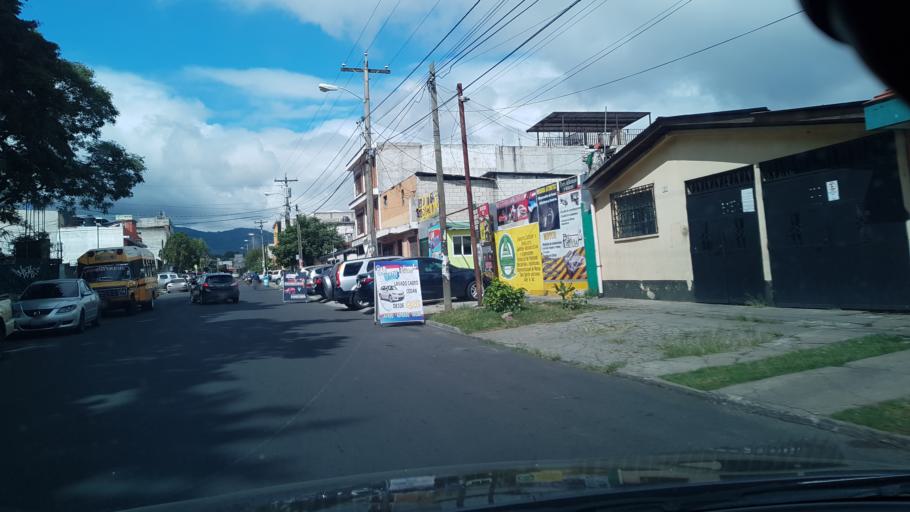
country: GT
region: Guatemala
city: Mixco
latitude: 14.6413
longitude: -90.5763
